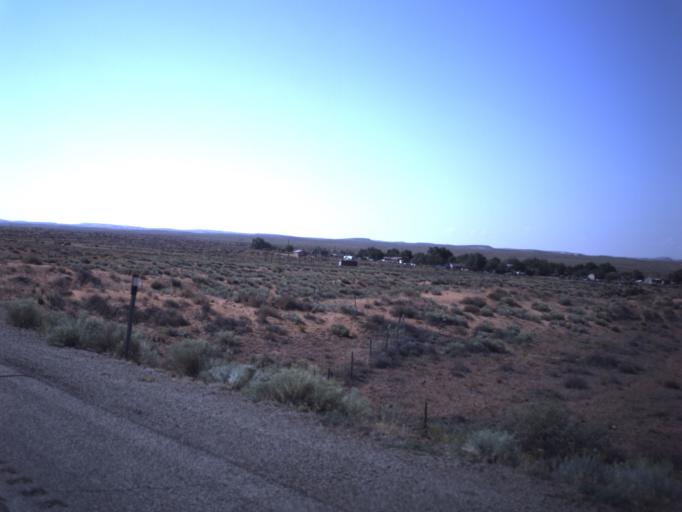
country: US
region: Utah
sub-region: San Juan County
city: Blanding
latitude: 37.2220
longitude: -109.6168
